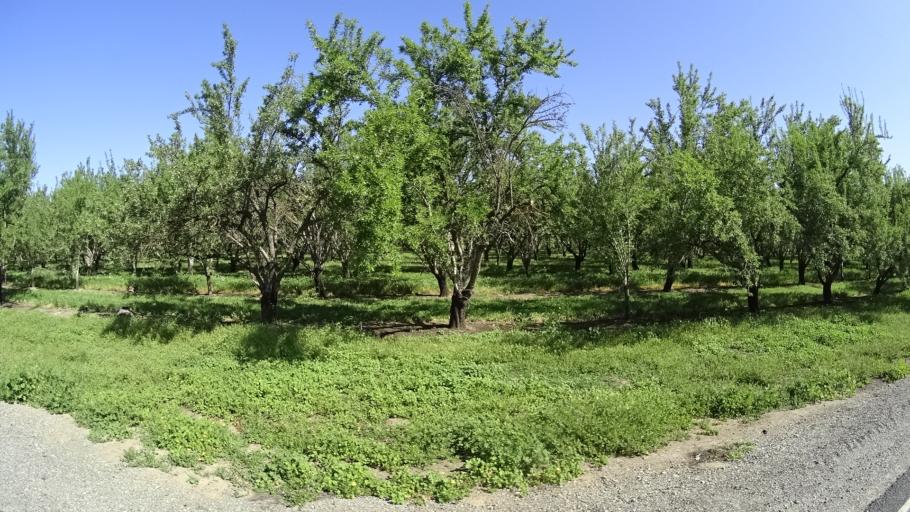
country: US
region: California
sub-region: Glenn County
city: Hamilton City
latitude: 39.6596
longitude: -122.0238
